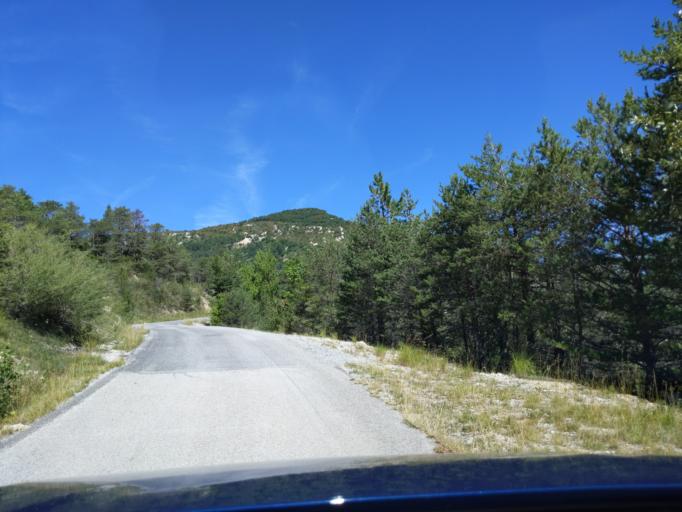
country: FR
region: Rhone-Alpes
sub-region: Departement de la Drome
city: Die
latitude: 44.6286
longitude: 5.5523
